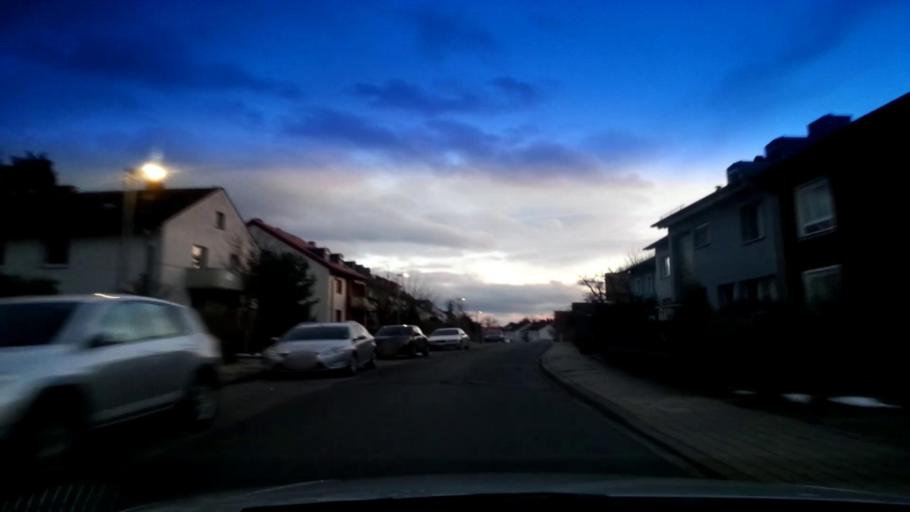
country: DE
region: Bavaria
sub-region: Upper Franconia
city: Gundelsheim
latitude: 49.9156
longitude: 10.9270
